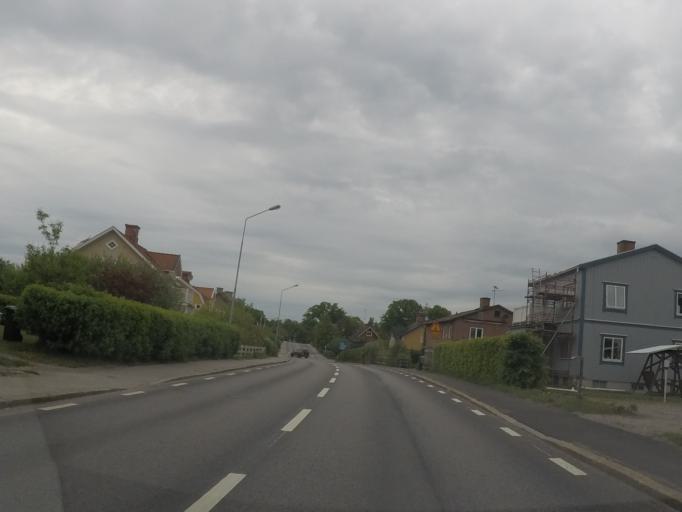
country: SE
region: Soedermanland
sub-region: Flens Kommun
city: Malmkoping
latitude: 59.0694
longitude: 16.8295
